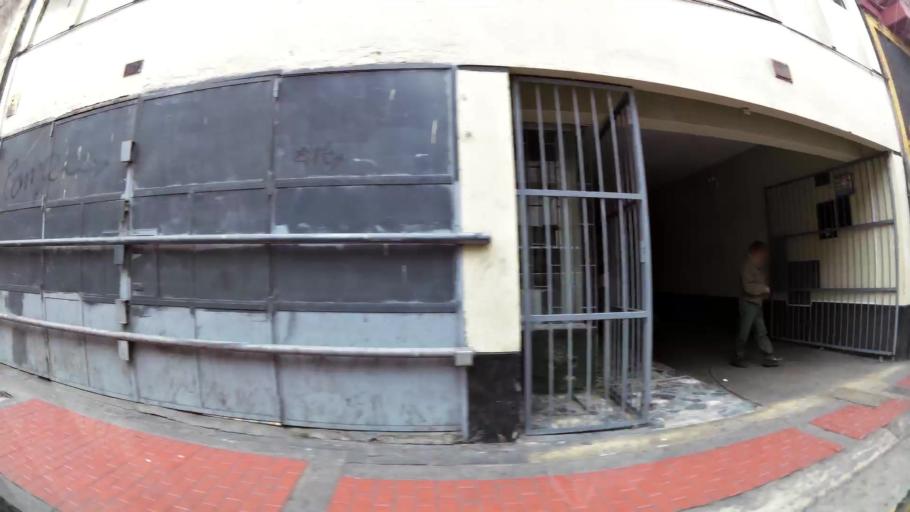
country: PE
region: Lima
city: Lima
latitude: -12.0543
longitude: -77.0354
